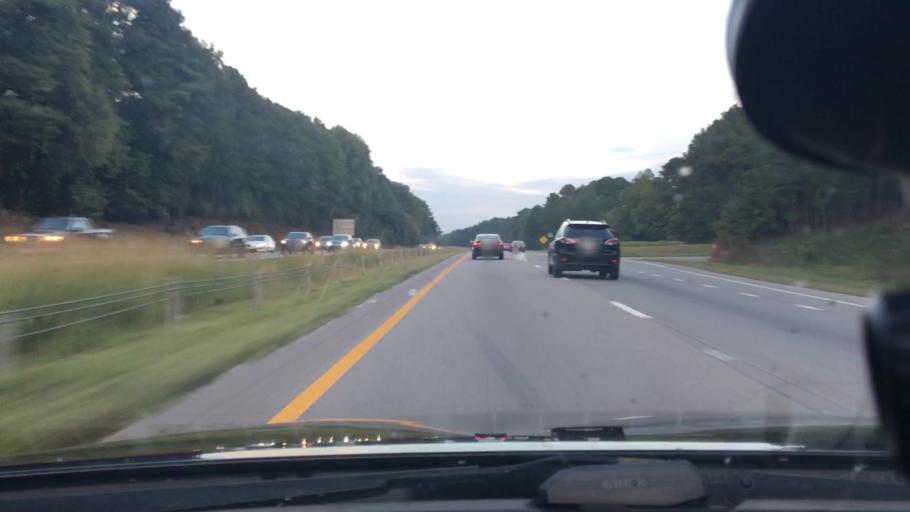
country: US
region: North Carolina
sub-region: Wake County
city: Apex
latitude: 35.7239
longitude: -78.8221
